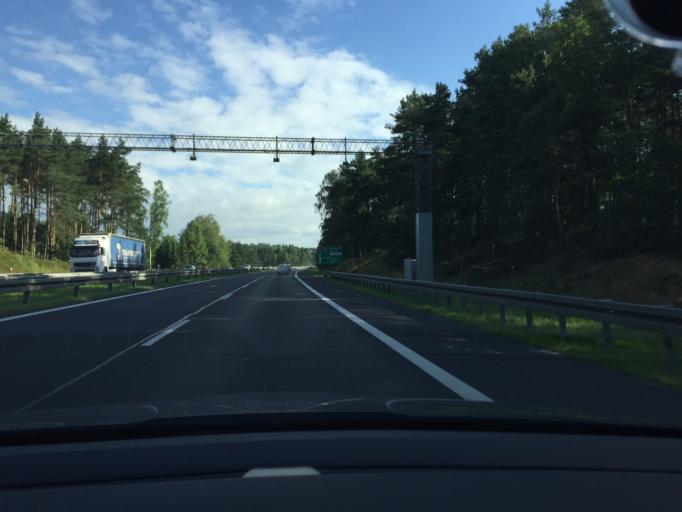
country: PL
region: West Pomeranian Voivodeship
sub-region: Powiat goleniowski
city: Goleniow
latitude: 53.5615
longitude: 14.7959
